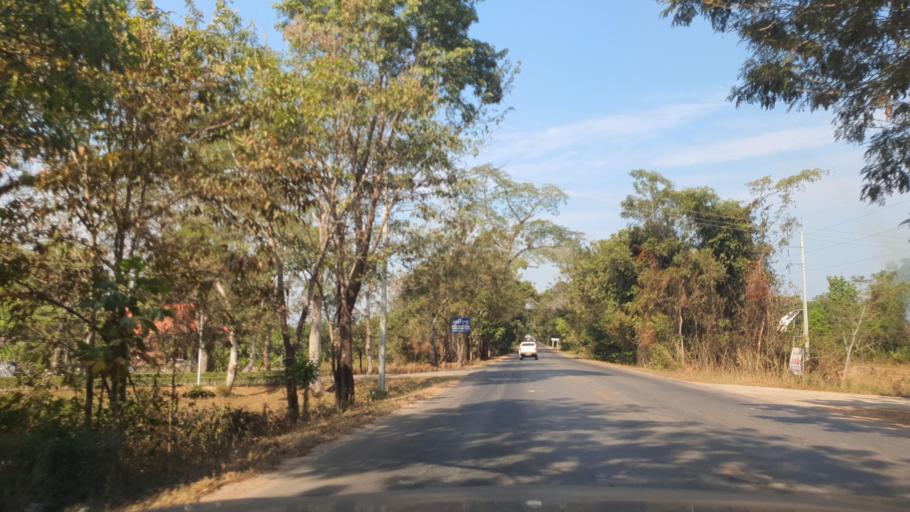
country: TH
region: Nakhon Phanom
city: Ban Phaeng
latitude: 18.0197
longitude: 104.1514
